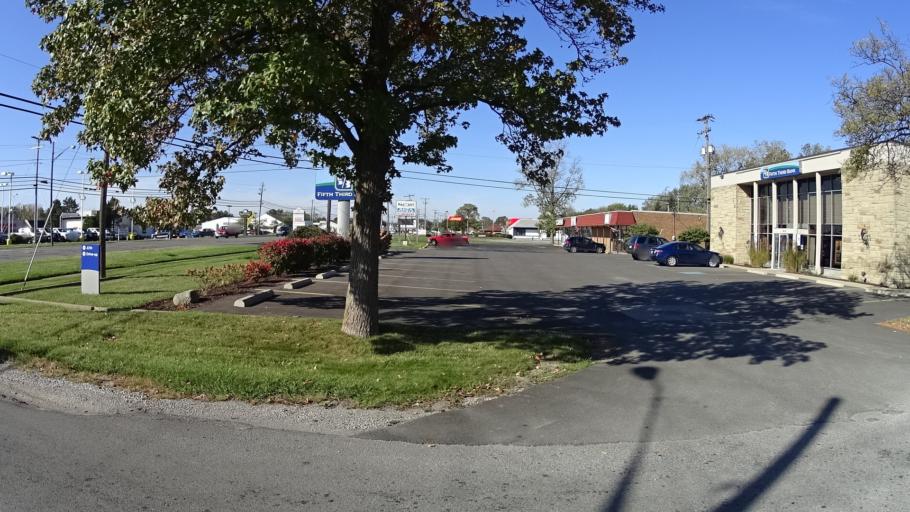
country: US
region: Ohio
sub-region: Lorain County
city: Vermilion-on-the-Lake
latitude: 41.4252
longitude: -82.3413
